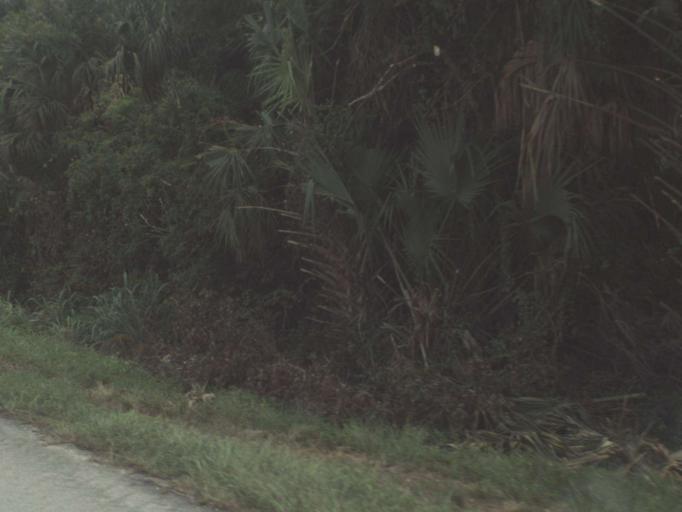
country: US
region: Florida
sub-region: Martin County
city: Indiantown
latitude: 27.0181
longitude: -80.6291
